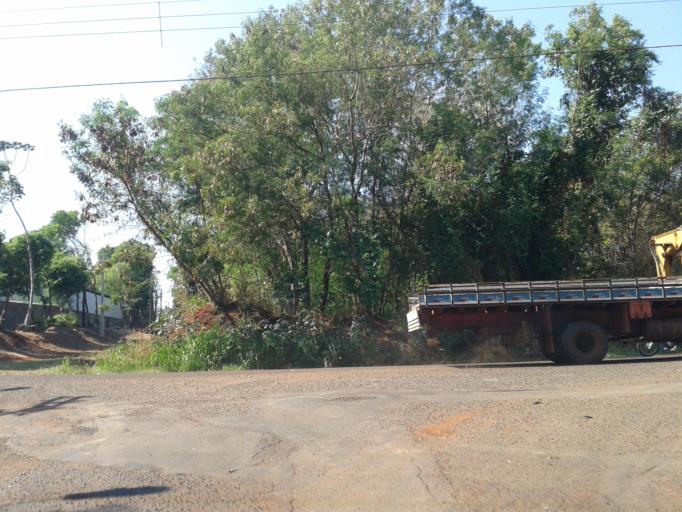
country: BR
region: Minas Gerais
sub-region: Ituiutaba
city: Ituiutaba
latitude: -18.9540
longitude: -49.4555
